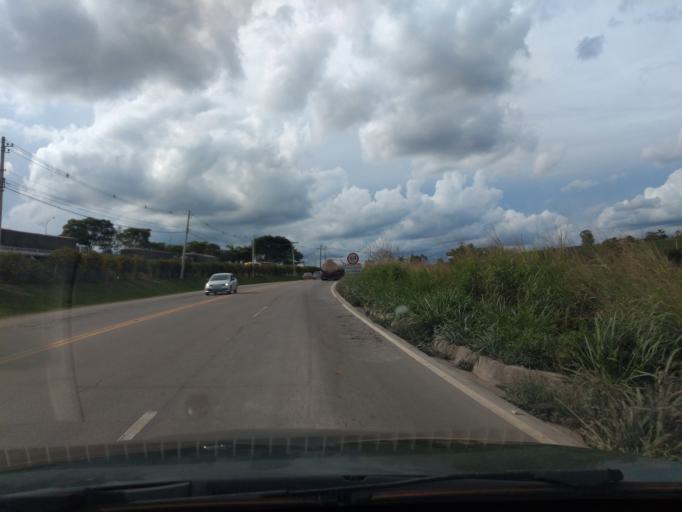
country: BR
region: Minas Gerais
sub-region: Varginha
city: Varginha
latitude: -21.6000
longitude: -45.4382
